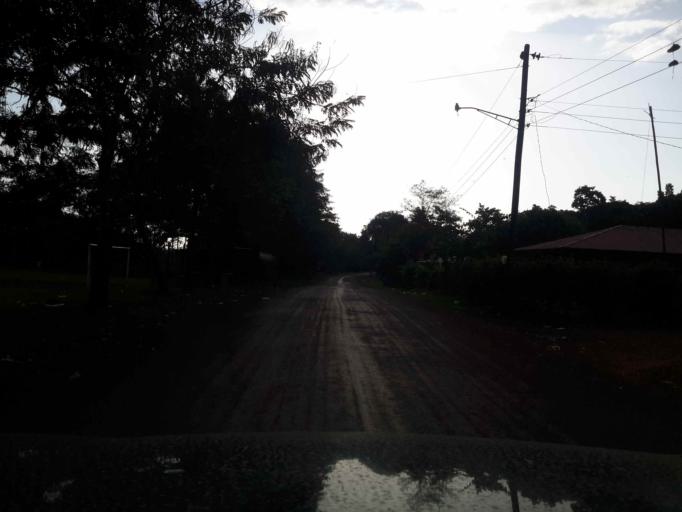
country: CR
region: Alajuela
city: Los Chiles
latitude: 11.1524
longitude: -84.6333
